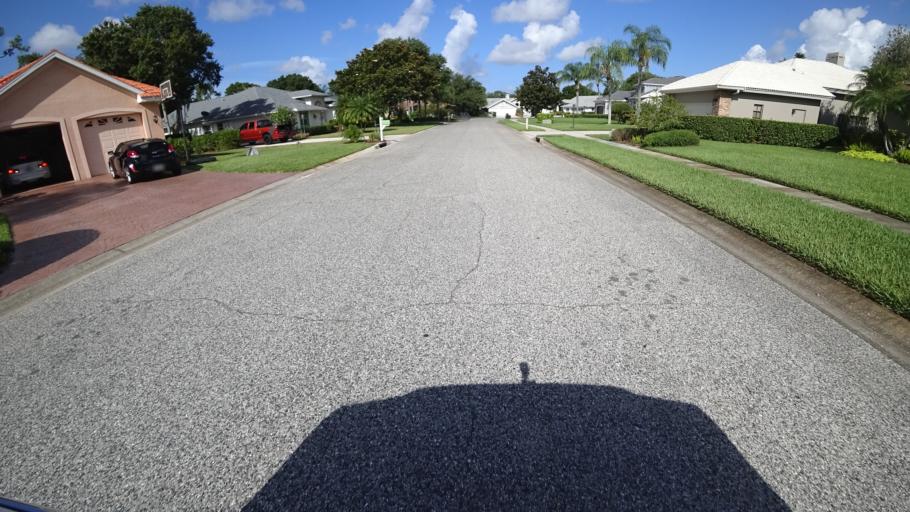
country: US
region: Florida
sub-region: Sarasota County
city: Desoto Lakes
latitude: 27.3969
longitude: -82.4832
